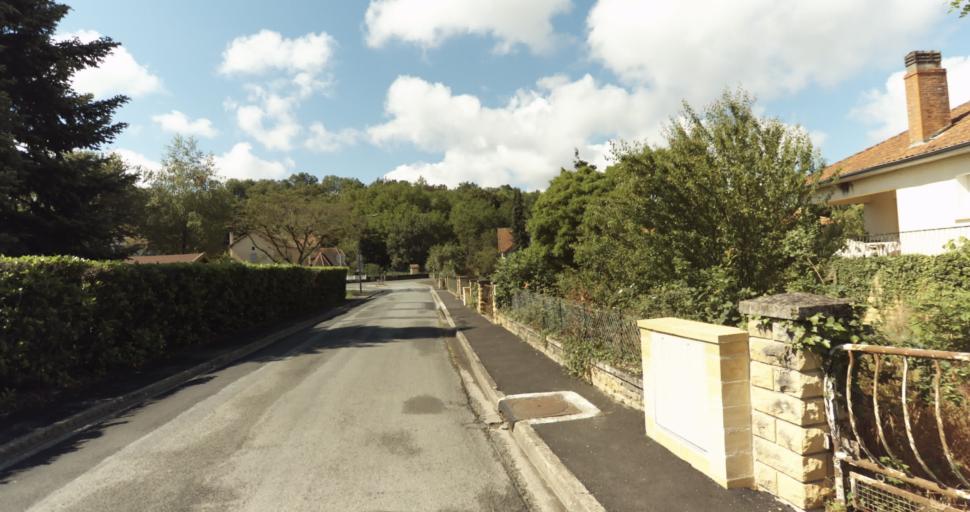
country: FR
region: Aquitaine
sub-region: Departement de la Dordogne
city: Le Bugue
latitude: 44.8422
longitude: 0.9062
